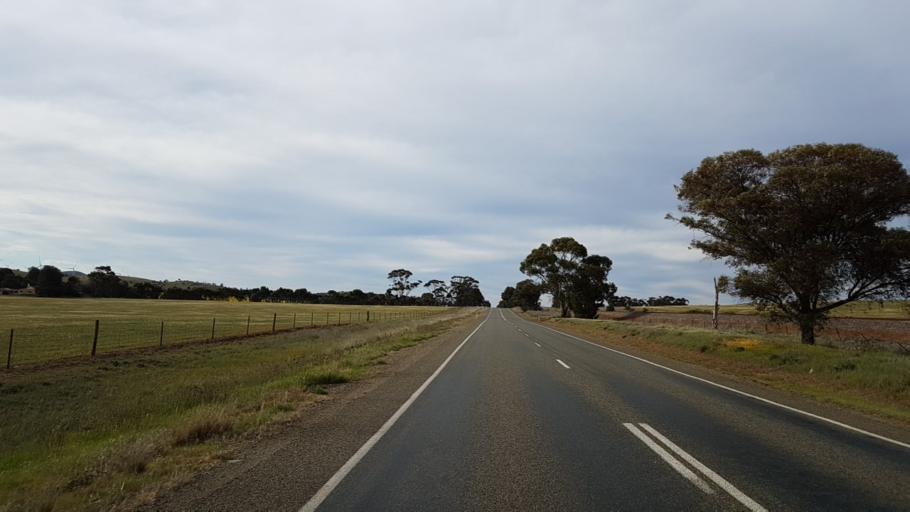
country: AU
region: South Australia
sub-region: Northern Areas
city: Jamestown
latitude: -33.1588
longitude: 138.6141
